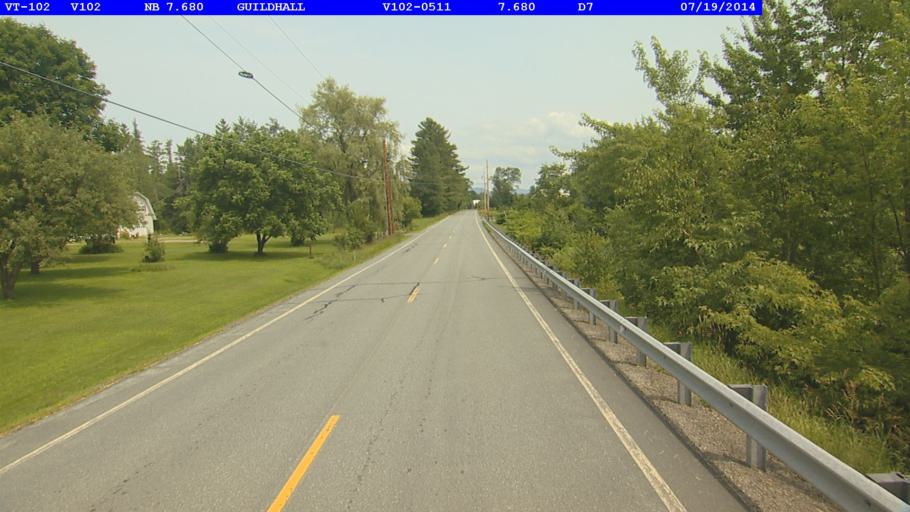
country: US
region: Vermont
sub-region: Essex County
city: Guildhall
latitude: 44.5703
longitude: -71.5584
